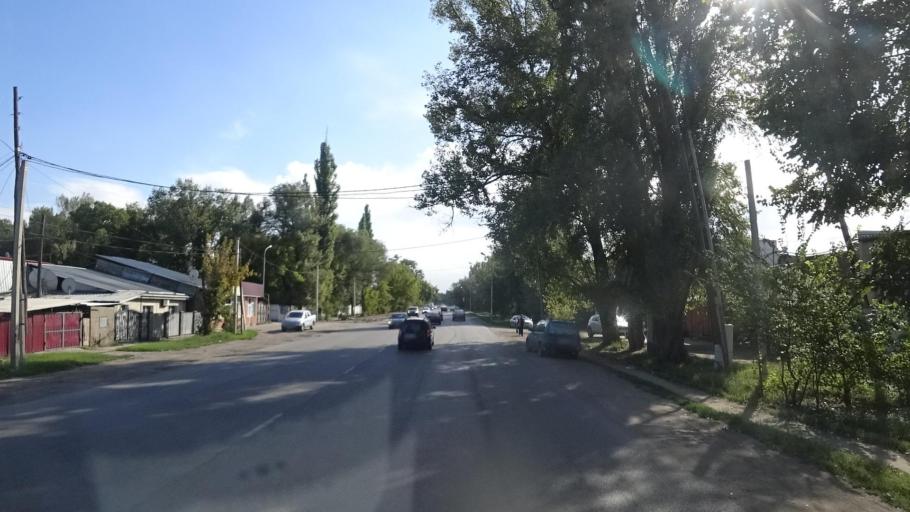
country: KZ
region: Almaty Oblysy
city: Energeticheskiy
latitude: 43.3839
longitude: 76.9993
